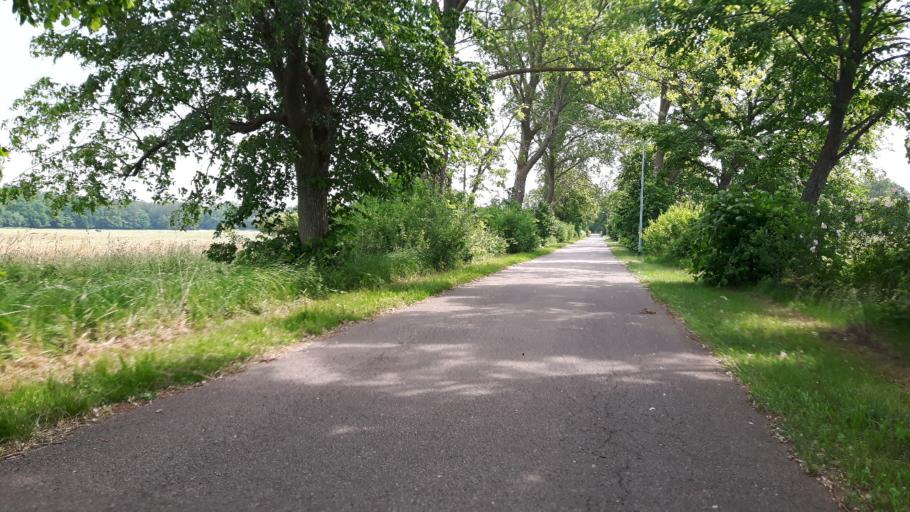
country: PL
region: Pomeranian Voivodeship
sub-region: Powiat leborski
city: Leba
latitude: 54.7528
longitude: 17.6070
